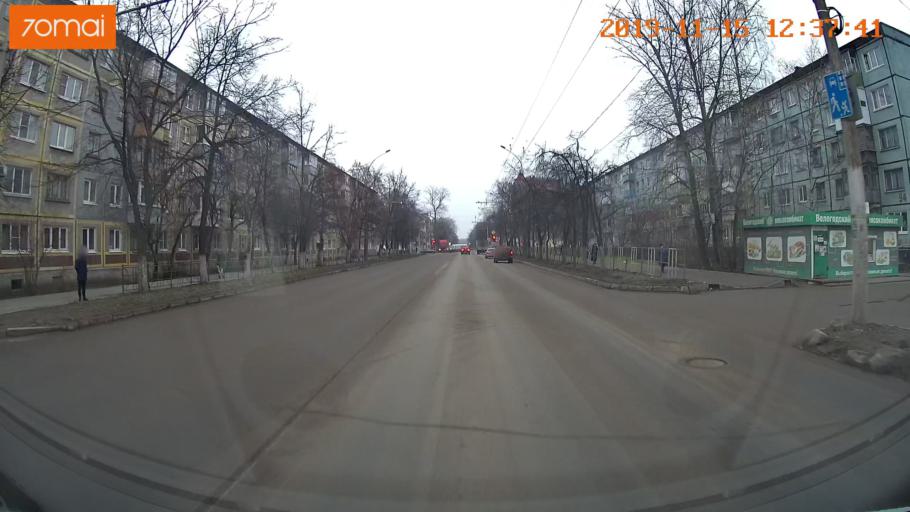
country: RU
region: Vologda
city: Vologda
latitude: 59.2074
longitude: 39.9017
